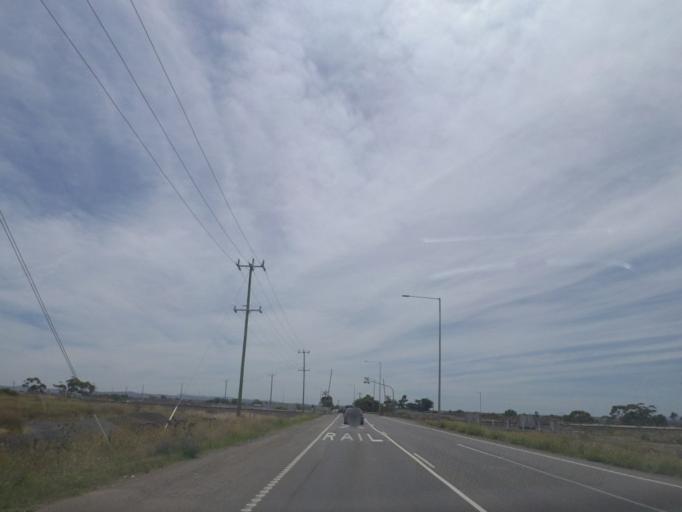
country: AU
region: Victoria
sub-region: Melton
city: Caroline Springs
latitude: -37.7530
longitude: 144.7038
